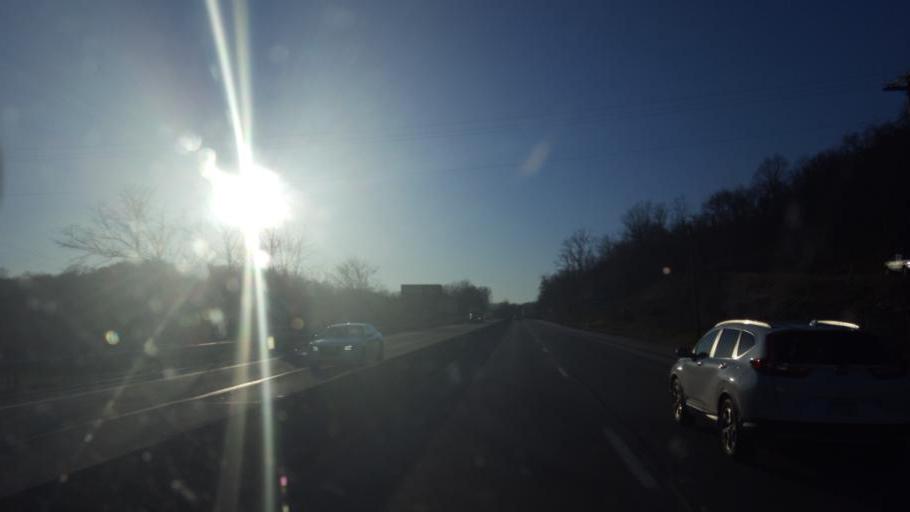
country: US
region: Pennsylvania
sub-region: Washington County
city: Charleroi
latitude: 40.1118
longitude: -79.9308
